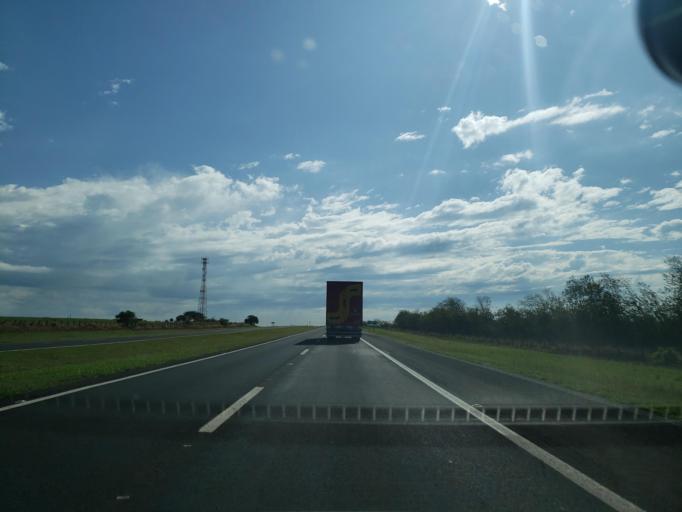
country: BR
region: Sao Paulo
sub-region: Pirajui
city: Pirajui
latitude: -21.9181
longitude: -49.5090
